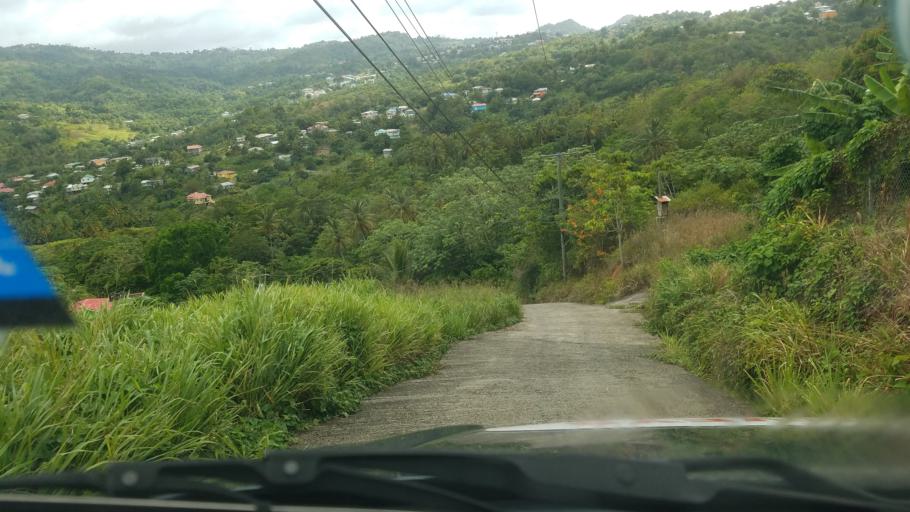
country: LC
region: Castries Quarter
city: Bisee
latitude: 14.0024
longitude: -60.9346
